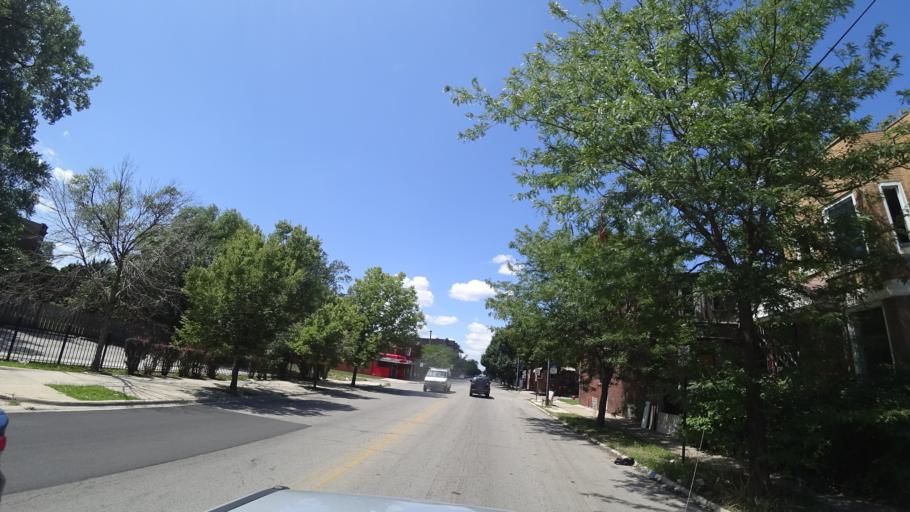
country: US
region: Illinois
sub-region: Cook County
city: Chicago
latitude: 41.7693
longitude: -87.6165
